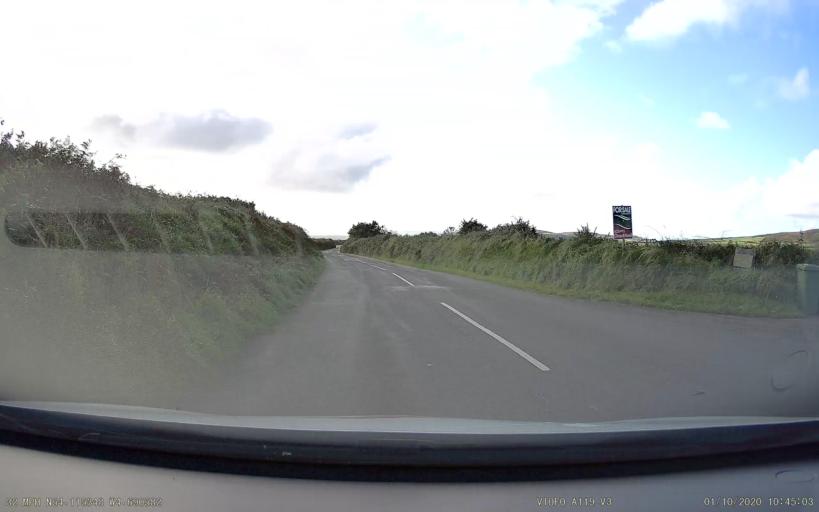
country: IM
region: Castletown
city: Castletown
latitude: 54.1153
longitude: -4.6906
